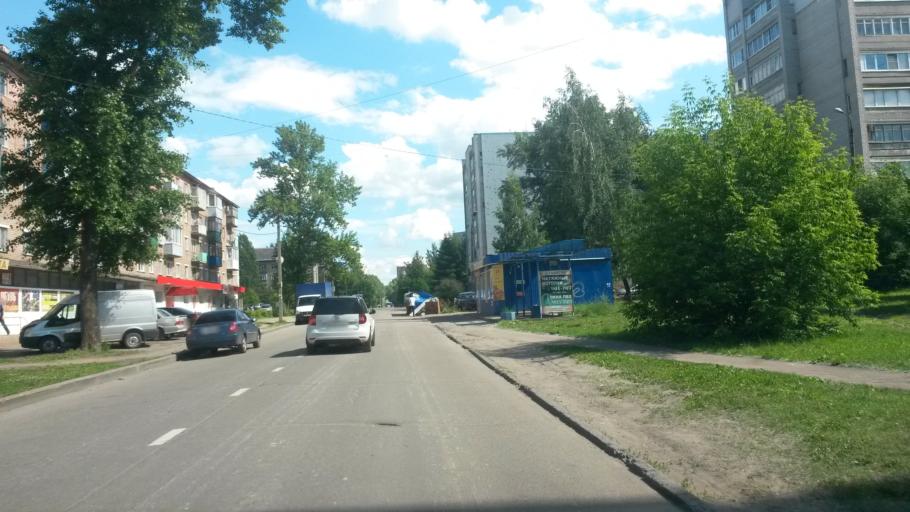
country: RU
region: Jaroslavl
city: Yaroslavl
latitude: 57.5830
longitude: 39.8288
